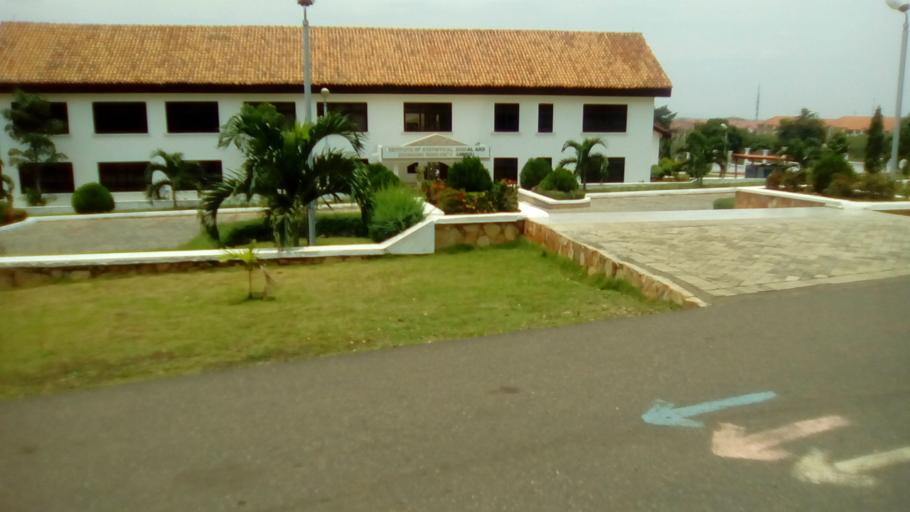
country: GH
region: Greater Accra
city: Medina Estates
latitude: 5.6547
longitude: -0.1844
